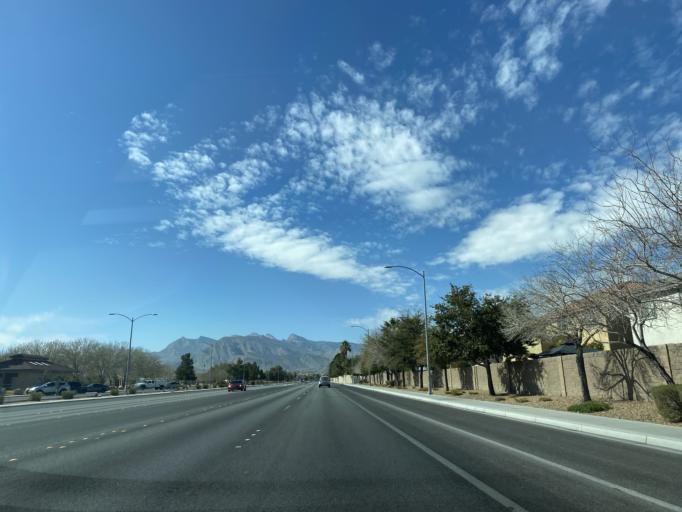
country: US
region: Nevada
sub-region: Clark County
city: Spring Valley
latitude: 36.2332
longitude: -115.2540
